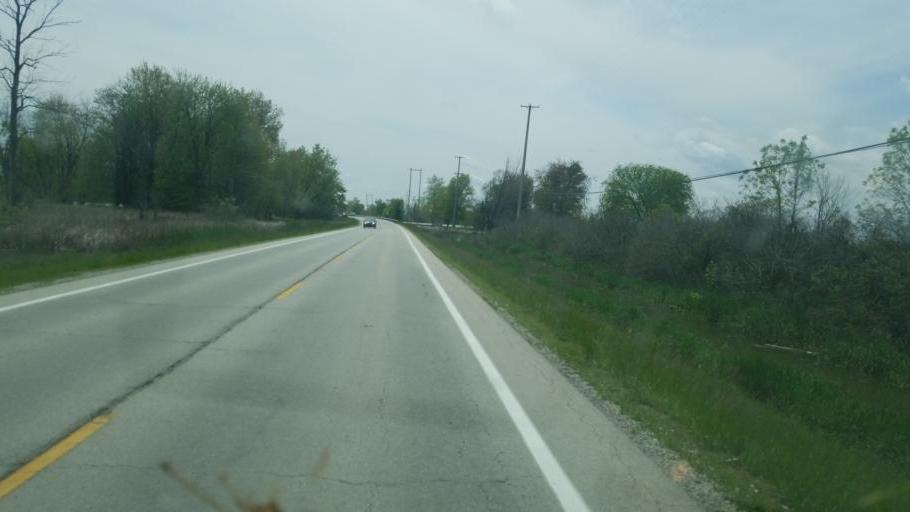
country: US
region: Ohio
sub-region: Ottawa County
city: Oak Harbor
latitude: 41.4548
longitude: -83.0534
